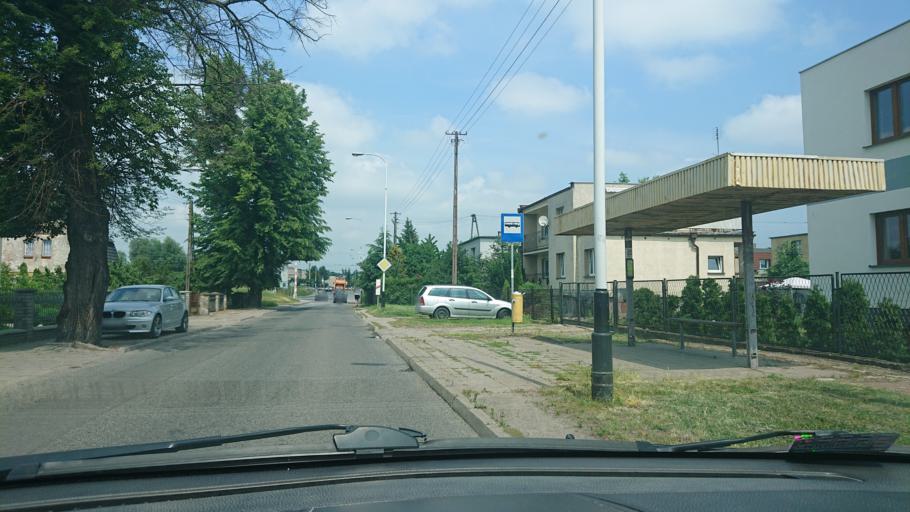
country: PL
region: Greater Poland Voivodeship
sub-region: Powiat gnieznienski
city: Gniezno
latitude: 52.5247
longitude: 17.5815
